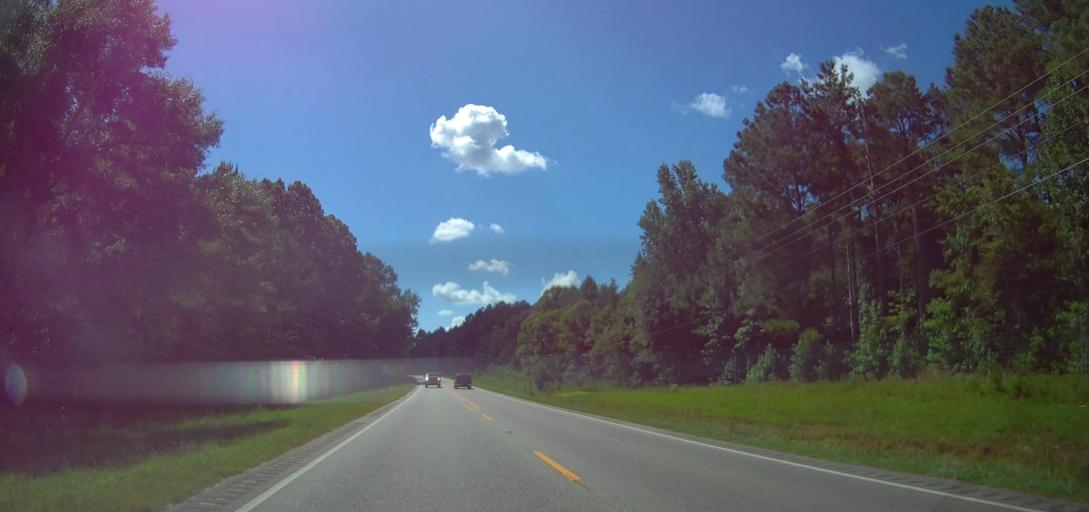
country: US
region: Alabama
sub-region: Macon County
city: Tuskegee
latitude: 32.3839
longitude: -85.8090
